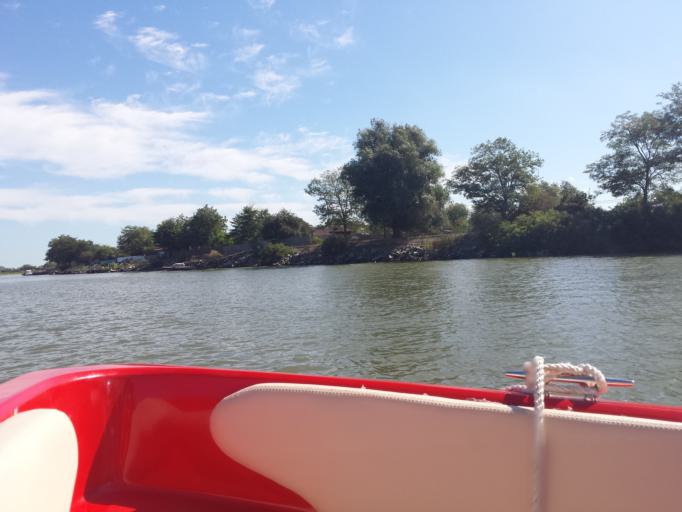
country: RO
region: Tulcea
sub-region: Comuna Crisan
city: Crisan
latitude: 45.2246
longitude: 29.2369
